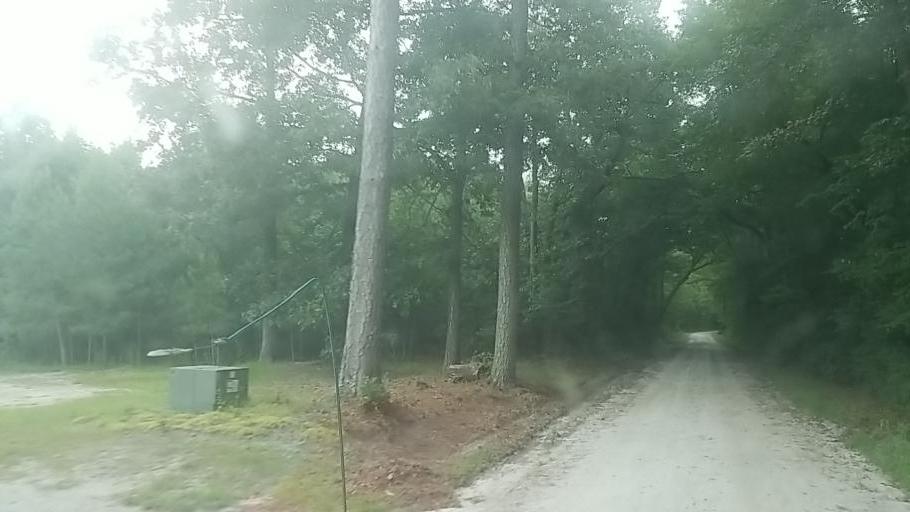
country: US
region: Maryland
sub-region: Wicomico County
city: Pittsville
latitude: 38.4440
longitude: -75.4410
